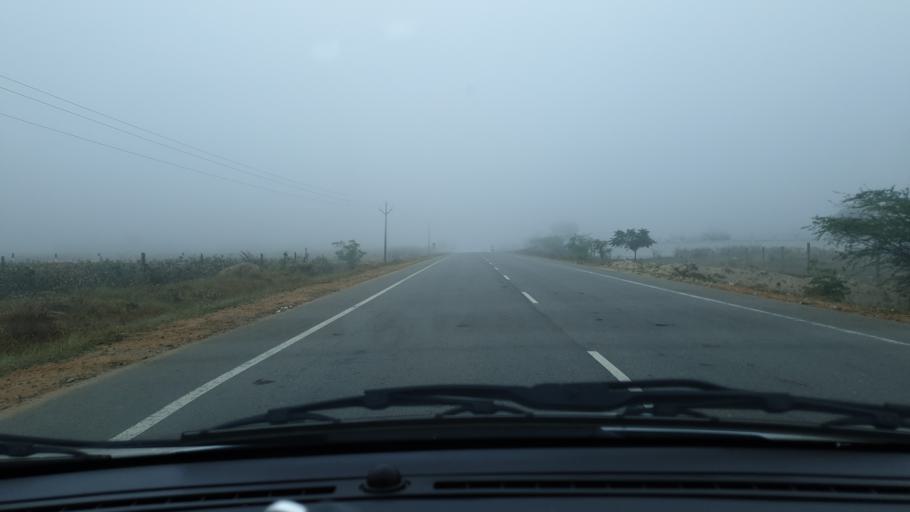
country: IN
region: Telangana
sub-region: Nalgonda
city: Devarkonda
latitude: 16.6181
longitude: 78.6733
